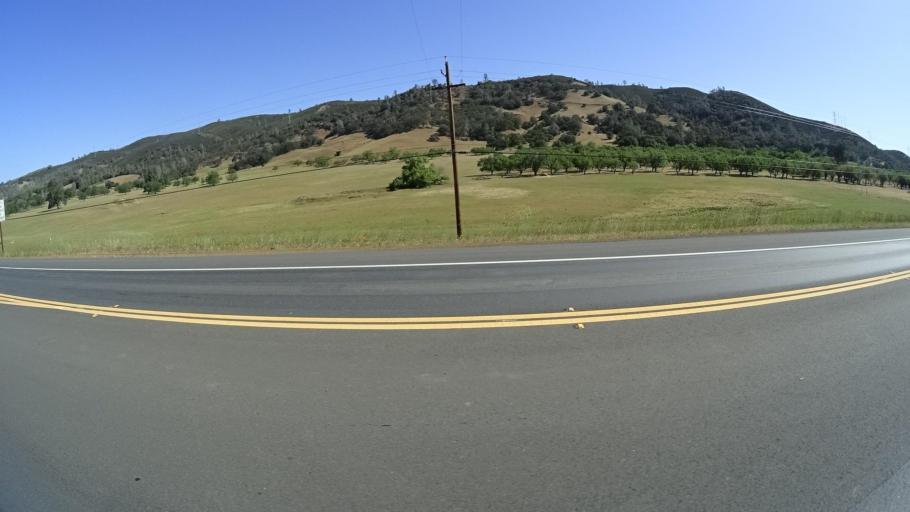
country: US
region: California
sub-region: Lake County
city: Clearlake
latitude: 39.0094
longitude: -122.6208
